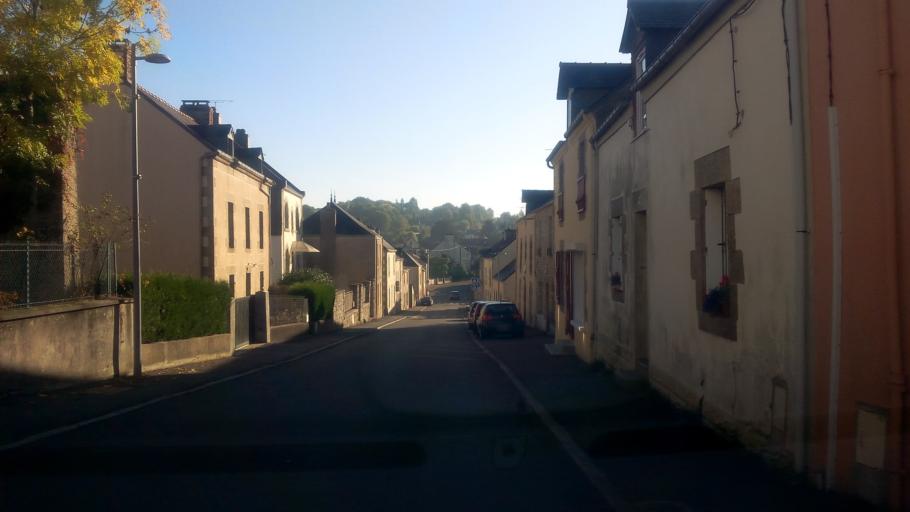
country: FR
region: Brittany
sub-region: Departement du Morbihan
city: Saint-Jean-la-Poterie
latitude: 47.6362
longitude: -2.1256
